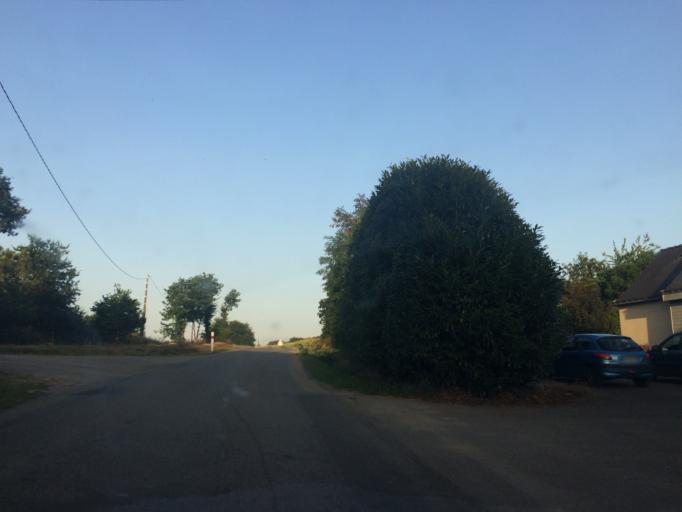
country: FR
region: Brittany
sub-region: Departement du Morbihan
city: Allaire
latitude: 47.6361
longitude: -2.2123
